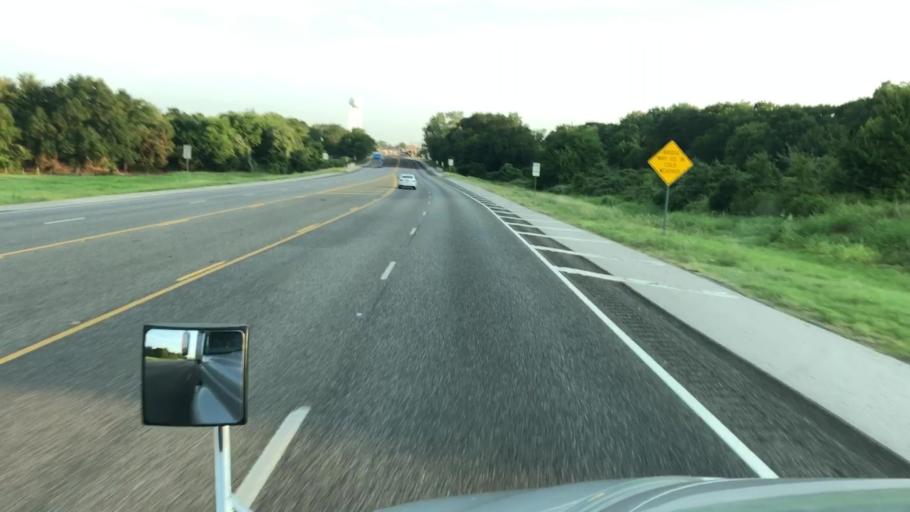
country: US
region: Texas
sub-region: Robertson County
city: Calvert
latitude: 30.9709
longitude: -96.6672
